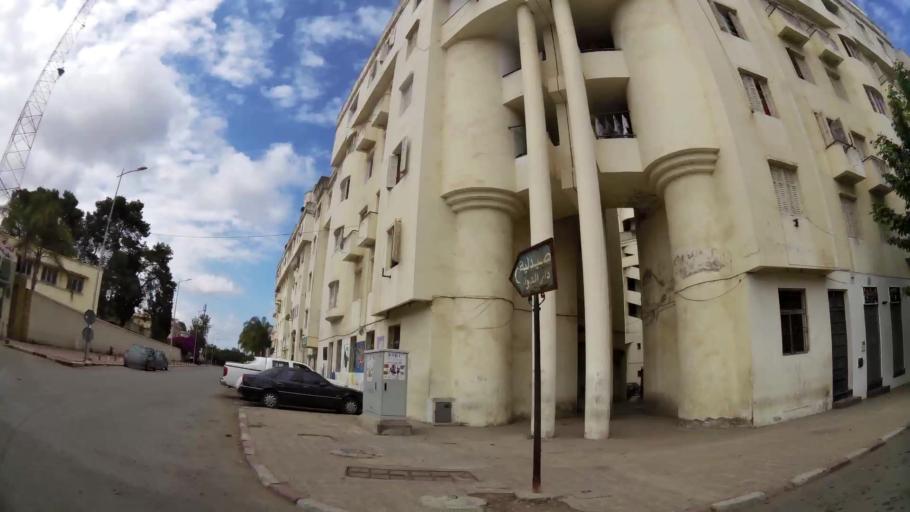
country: MA
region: Gharb-Chrarda-Beni Hssen
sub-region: Kenitra Province
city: Kenitra
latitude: 34.2542
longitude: -6.5860
